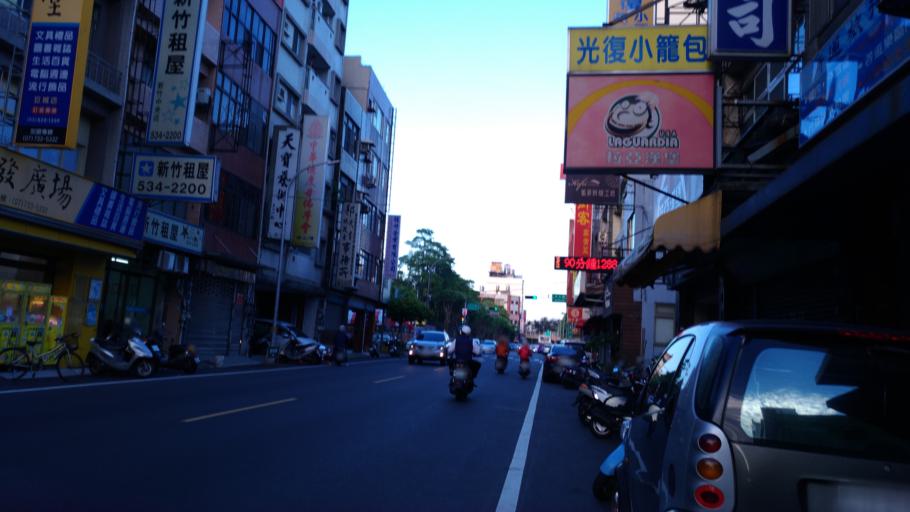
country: TW
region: Taiwan
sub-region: Hsinchu
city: Hsinchu
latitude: 24.8107
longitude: 120.9787
